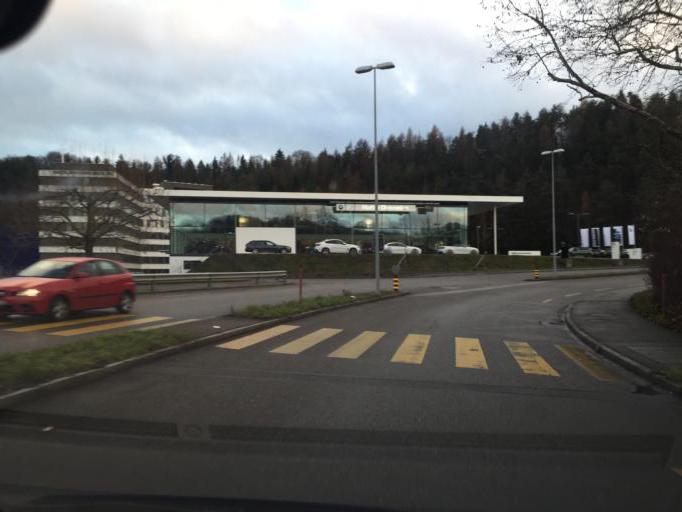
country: CH
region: Schaffhausen
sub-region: Bezirk Reiat
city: Stetten
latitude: 47.7143
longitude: 8.6580
